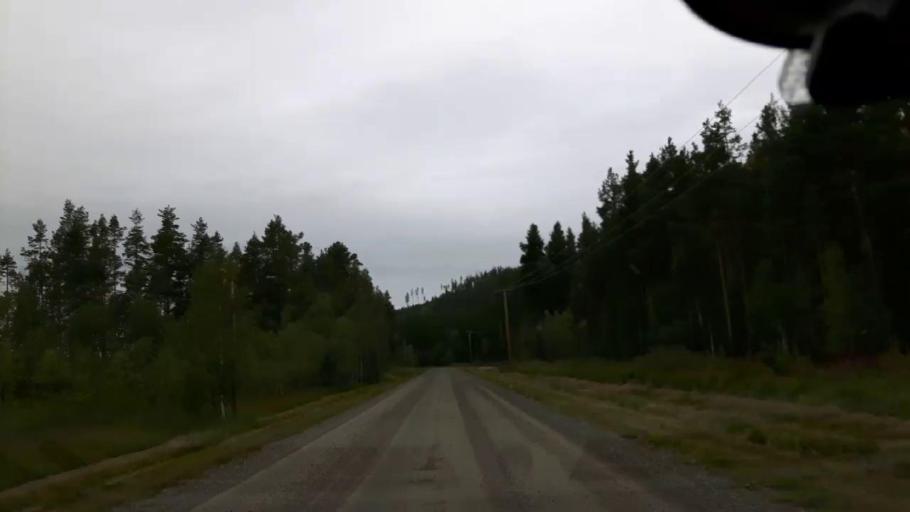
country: SE
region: Vaesternorrland
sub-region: Ange Kommun
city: Fransta
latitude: 62.7851
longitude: 16.0660
